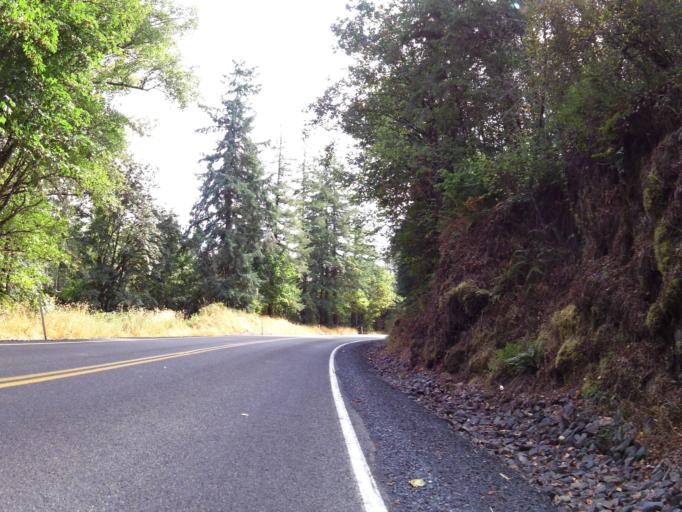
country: US
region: Washington
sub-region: Lewis County
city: Napavine
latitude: 46.5520
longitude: -122.9566
